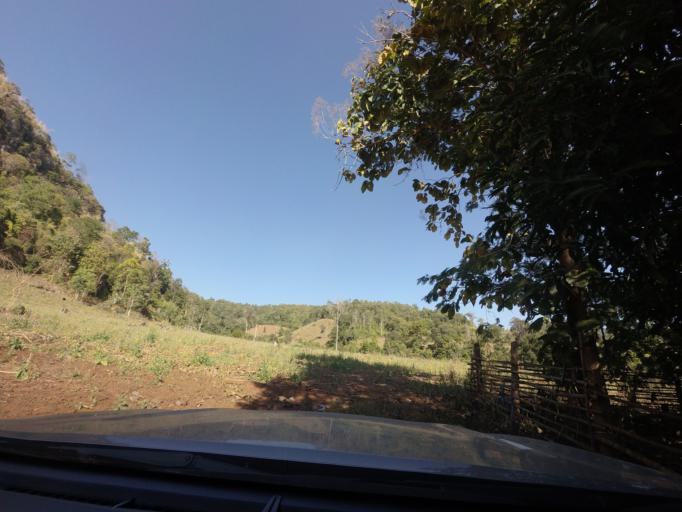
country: TH
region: Lampang
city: Chae Hom
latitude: 18.6194
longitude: 99.6806
